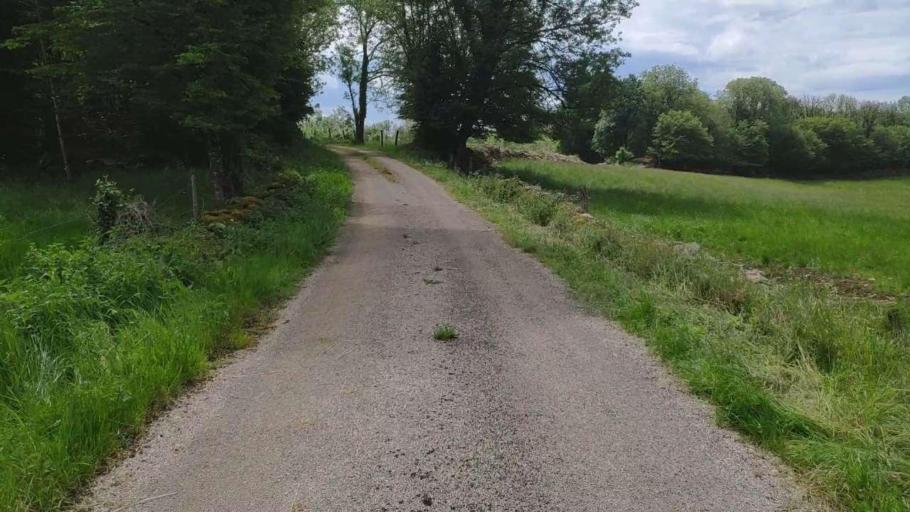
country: FR
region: Franche-Comte
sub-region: Departement du Jura
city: Perrigny
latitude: 46.7426
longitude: 5.6424
